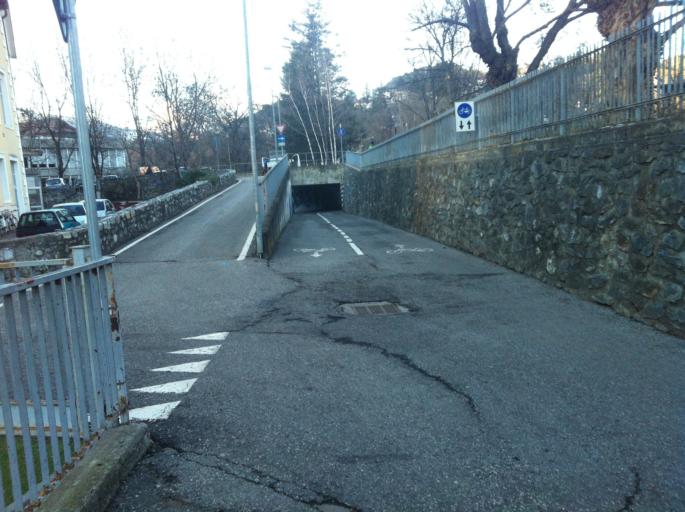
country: IT
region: Trentino-Alto Adige
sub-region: Bolzano
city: Bressanone
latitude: 46.7135
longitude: 11.6602
